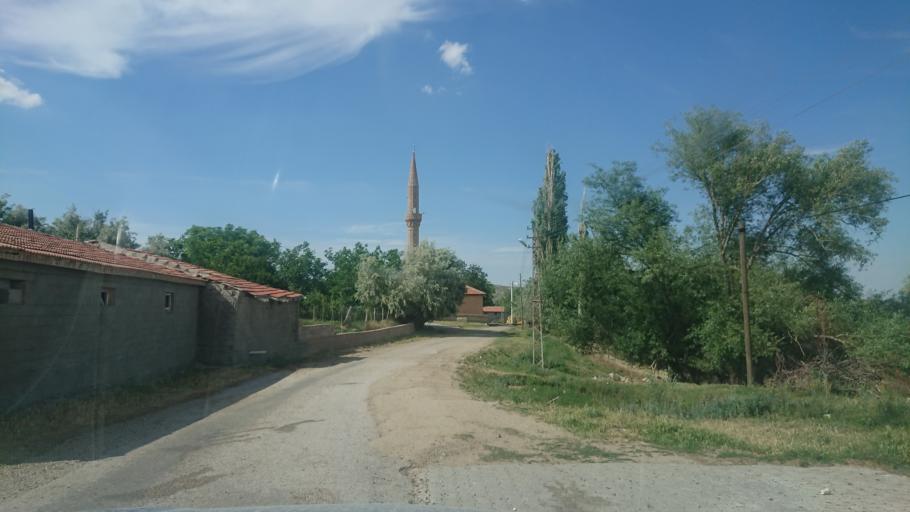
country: TR
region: Aksaray
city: Ortakoy
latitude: 38.8216
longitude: 34.0046
